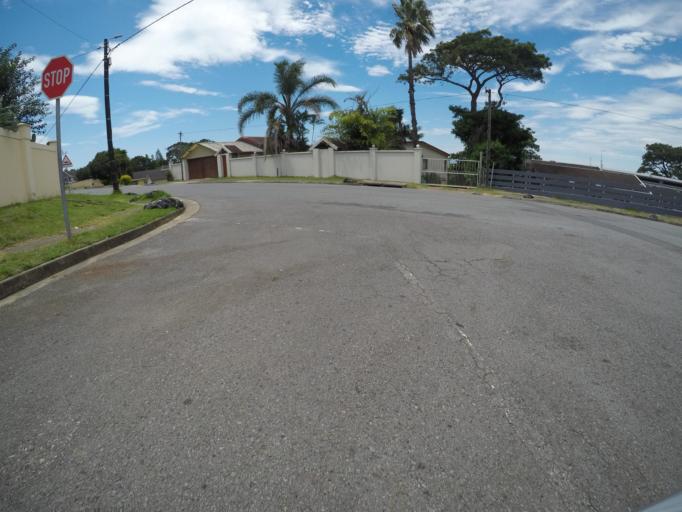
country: ZA
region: Eastern Cape
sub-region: Buffalo City Metropolitan Municipality
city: East London
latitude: -33.0396
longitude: 27.8535
